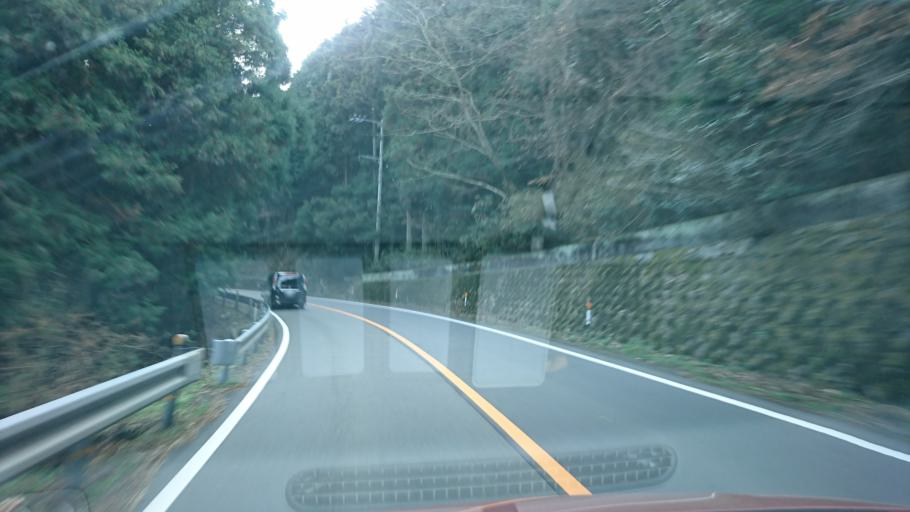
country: JP
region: Ehime
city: Hojo
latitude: 33.9711
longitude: 132.9023
